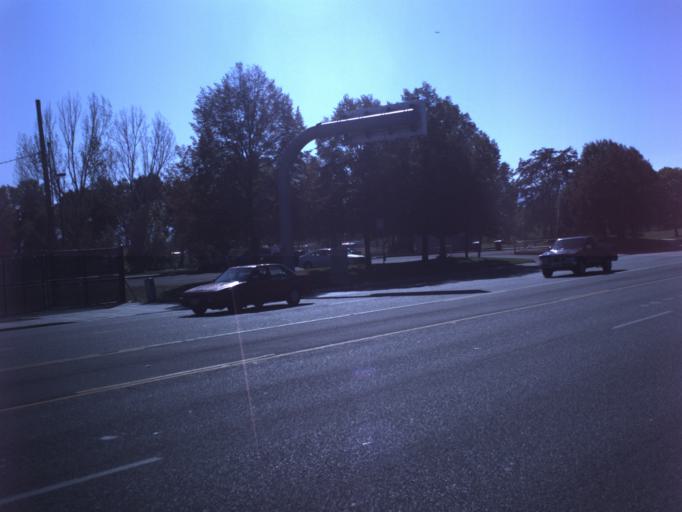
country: US
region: Utah
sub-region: Salt Lake County
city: Centerfield
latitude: 40.6995
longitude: -111.9219
